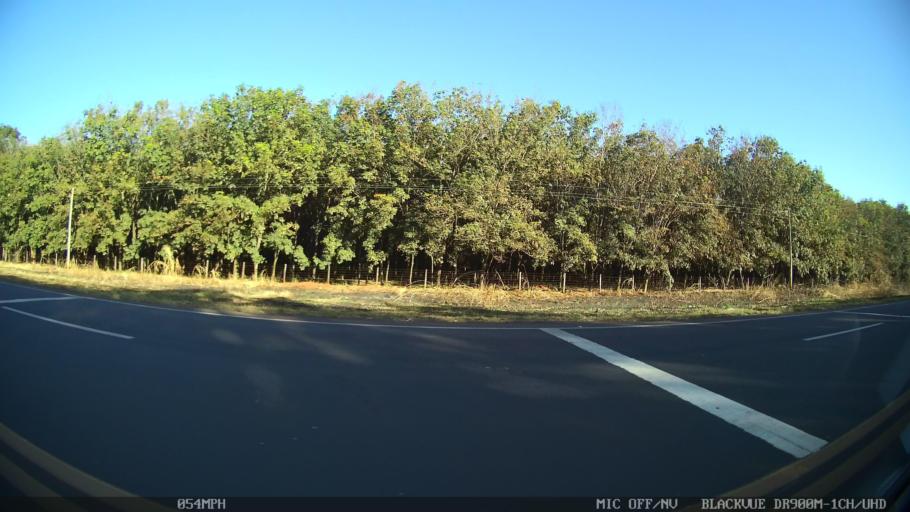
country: BR
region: Sao Paulo
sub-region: Guapiacu
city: Guapiacu
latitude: -20.7621
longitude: -49.1816
